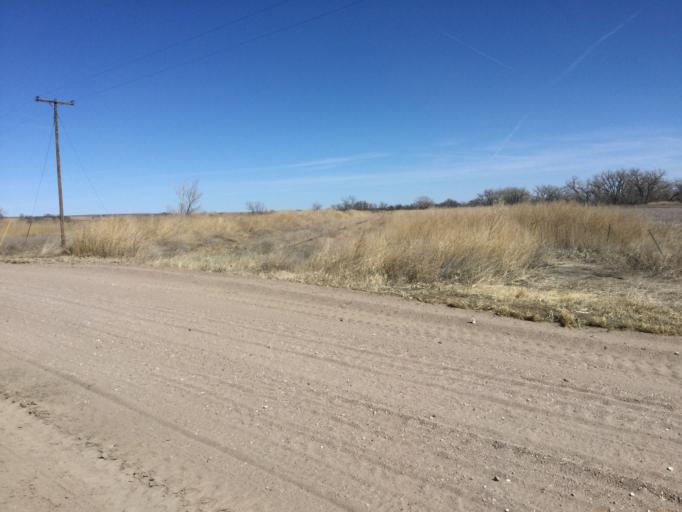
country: US
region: Kansas
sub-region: Rawlins County
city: Atwood
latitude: 39.8904
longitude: -100.8516
